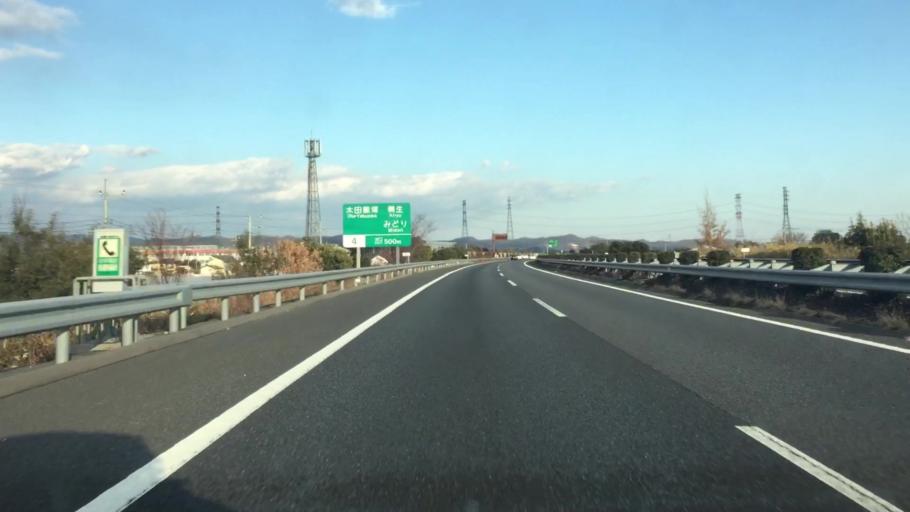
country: JP
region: Gunma
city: Isesaki
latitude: 36.3461
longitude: 139.2682
